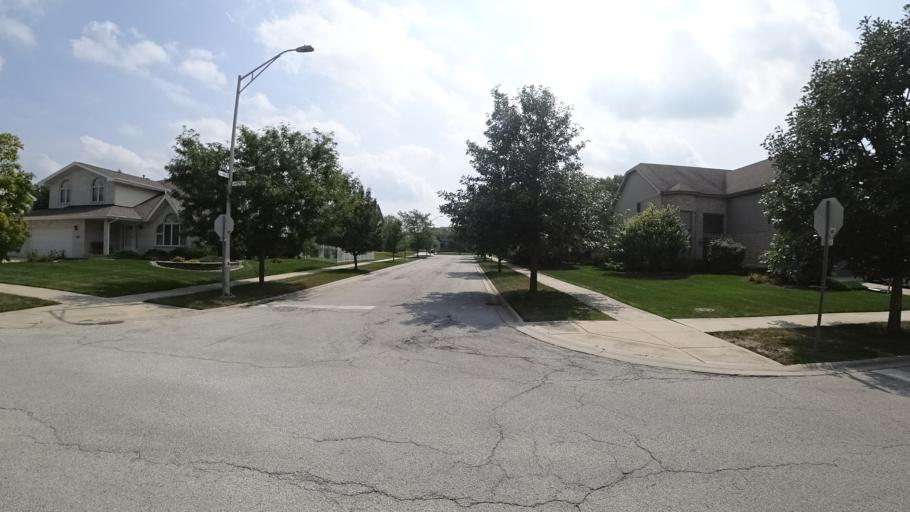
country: US
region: Illinois
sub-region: Will County
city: Goodings Grove
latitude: 41.6318
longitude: -87.9059
